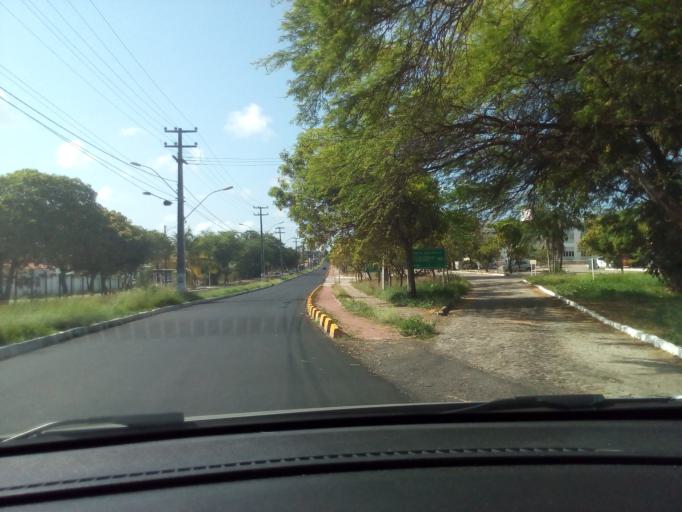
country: BR
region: Rio Grande do Norte
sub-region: Natal
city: Natal
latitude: -5.8429
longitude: -35.2028
